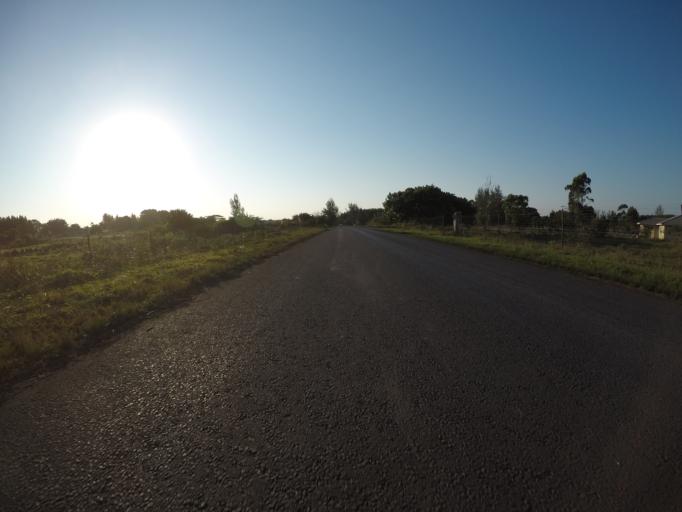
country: ZA
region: KwaZulu-Natal
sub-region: uThungulu District Municipality
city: KwaMbonambi
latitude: -28.6856
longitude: 32.2062
